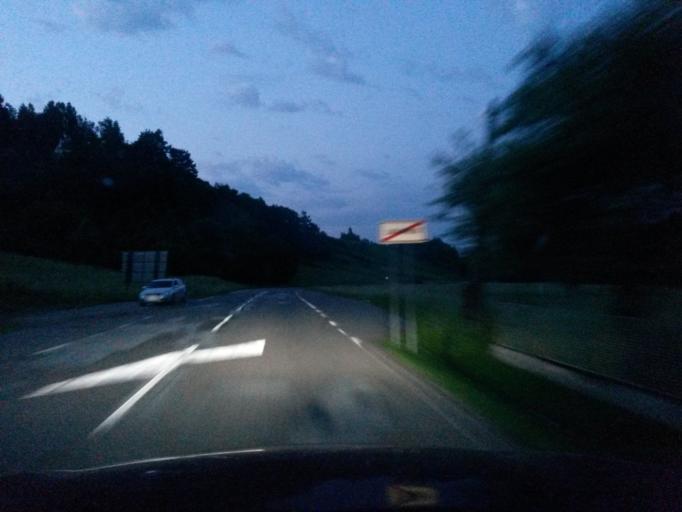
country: UA
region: Zakarpattia
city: Velykyi Bereznyi
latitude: 48.9223
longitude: 22.3195
